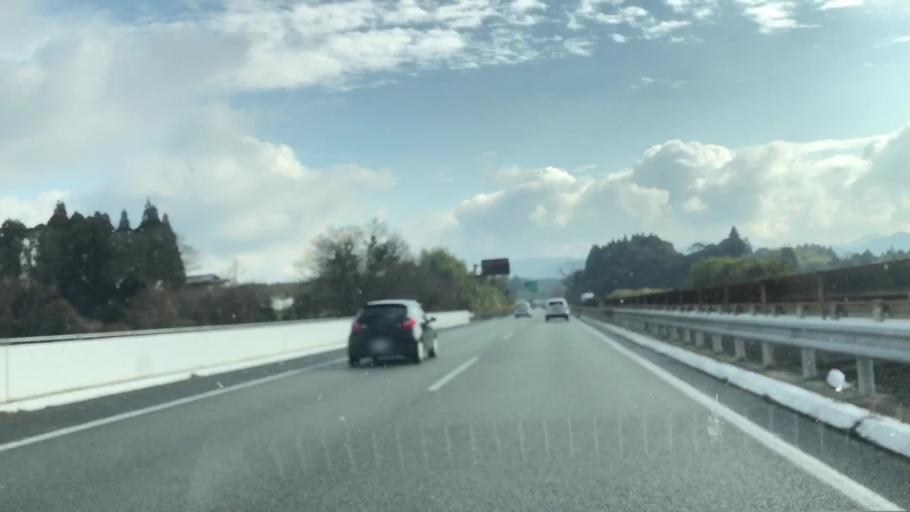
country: JP
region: Kumamoto
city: Tamana
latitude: 32.9915
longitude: 130.6023
